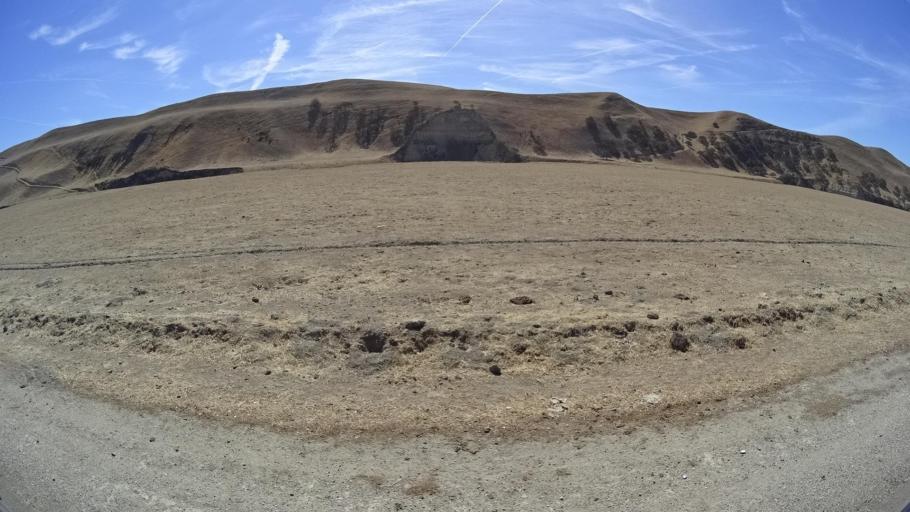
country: US
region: California
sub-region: San Luis Obispo County
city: Lake Nacimiento
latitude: 36.0321
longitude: -120.8577
